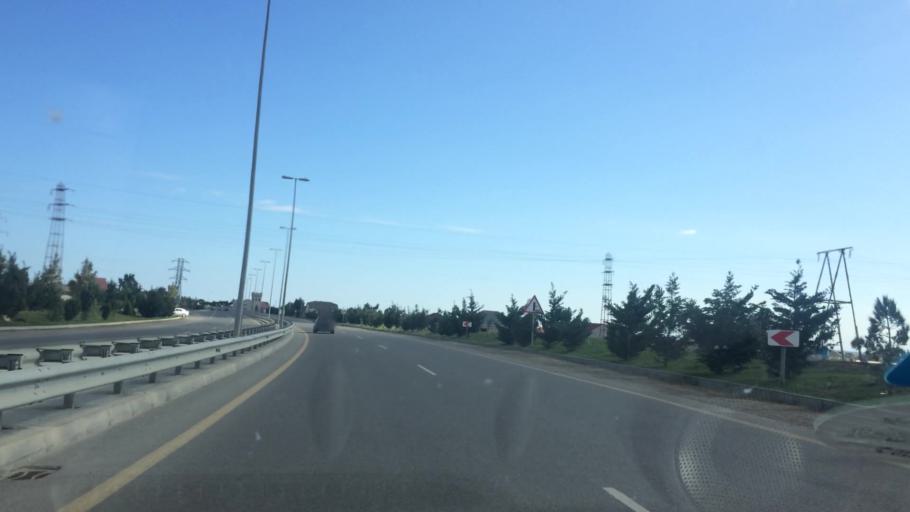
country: AZ
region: Baki
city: Zyrya
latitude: 40.3980
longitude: 50.3281
